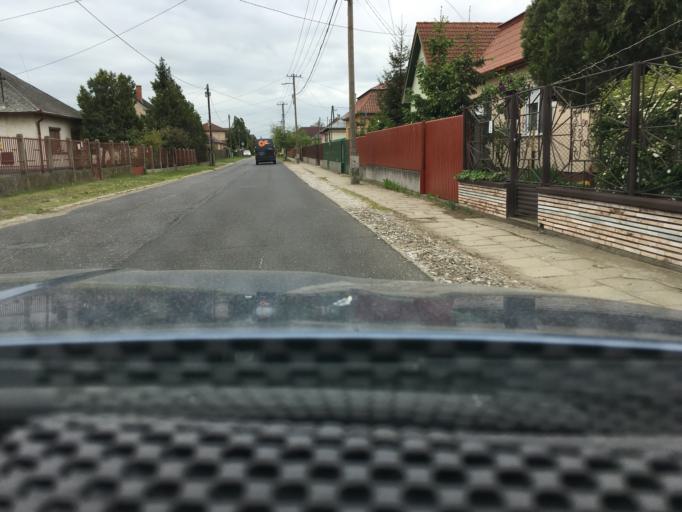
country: HU
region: Hajdu-Bihar
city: Debrecen
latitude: 47.5446
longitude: 21.6661
